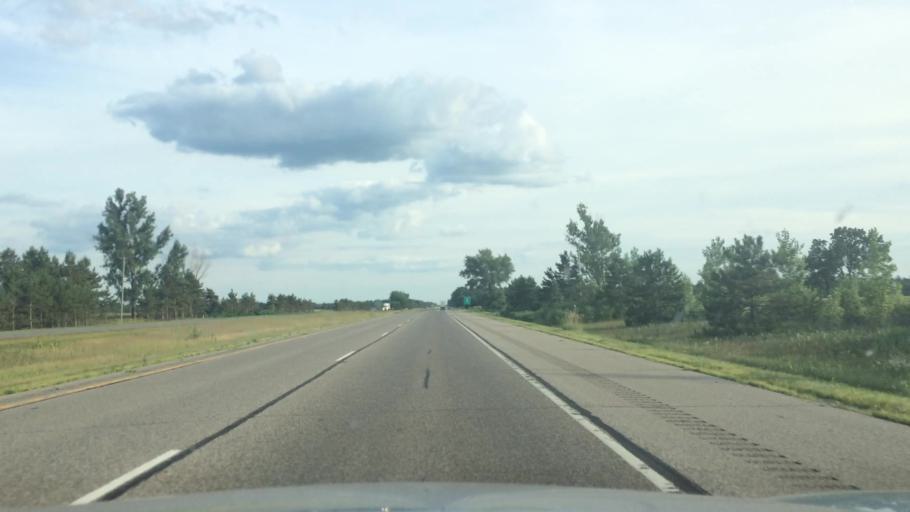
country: US
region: Wisconsin
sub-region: Portage County
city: Plover
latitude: 44.2819
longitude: -89.5237
